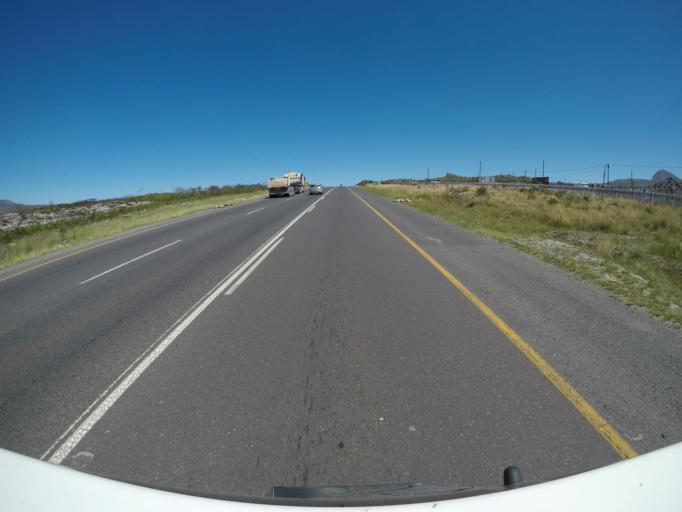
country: ZA
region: Western Cape
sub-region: Overberg District Municipality
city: Grabouw
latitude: -34.1607
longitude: 18.9801
